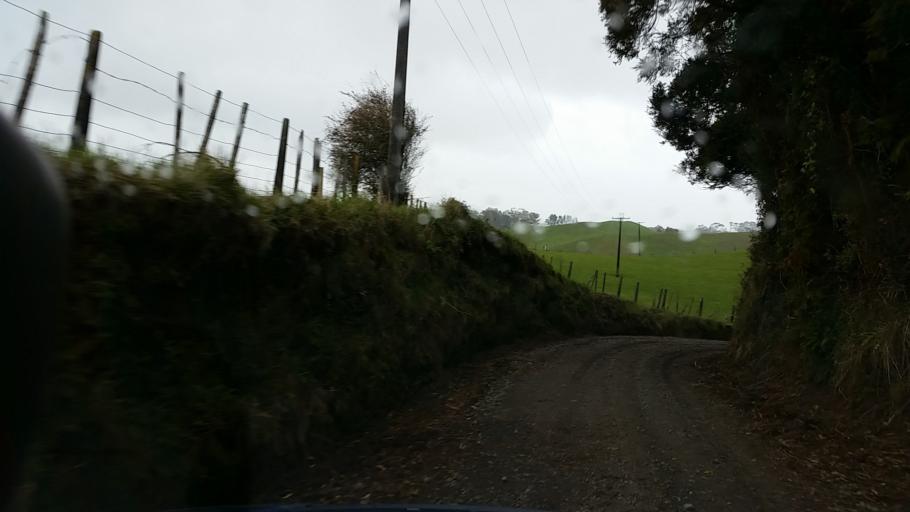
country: NZ
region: Taranaki
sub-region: South Taranaki District
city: Eltham
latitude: -39.2765
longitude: 174.3394
